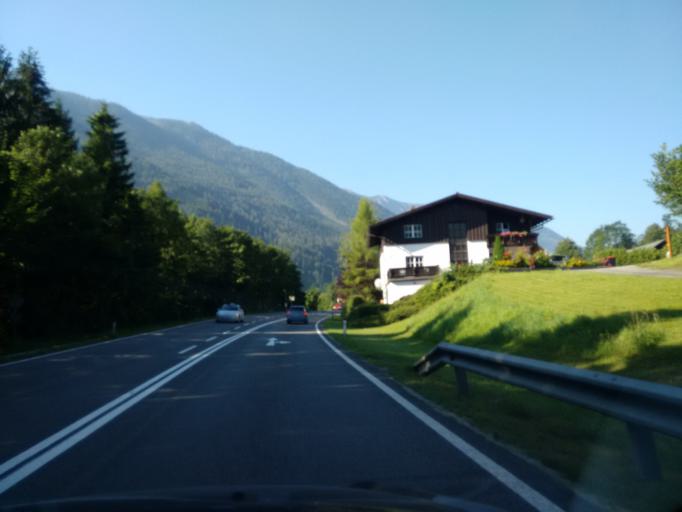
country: AT
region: Upper Austria
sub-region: Politischer Bezirk Gmunden
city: Ebensee
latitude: 47.7769
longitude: 13.7291
